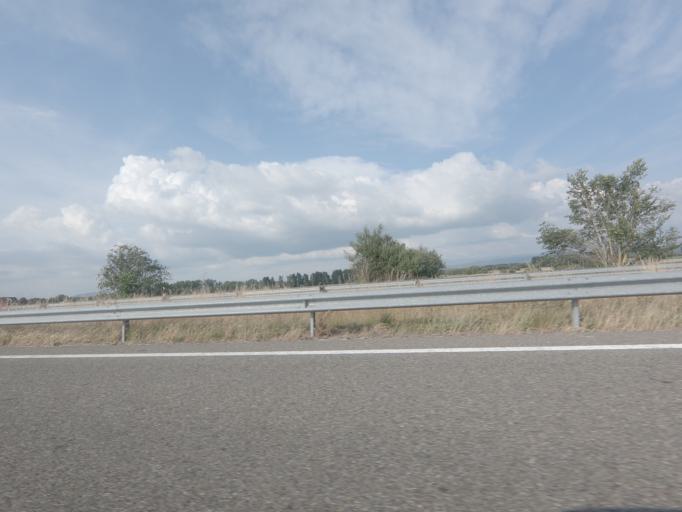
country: ES
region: Galicia
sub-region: Provincia de Ourense
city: Xinzo de Limia
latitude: 42.0969
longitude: -7.7276
